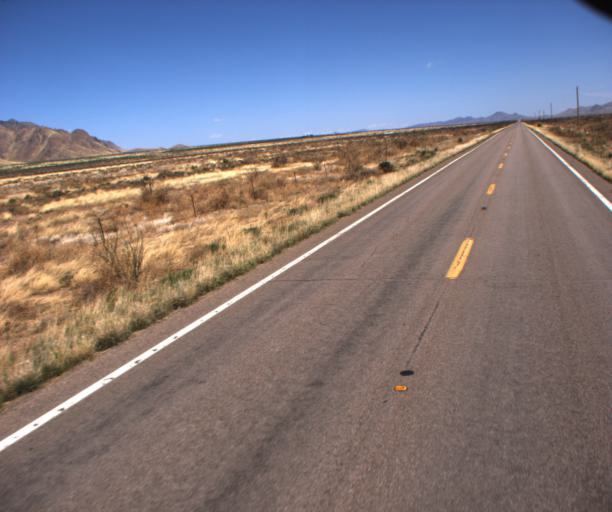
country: US
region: Arizona
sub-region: Cochise County
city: Douglas
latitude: 31.7254
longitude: -109.1086
